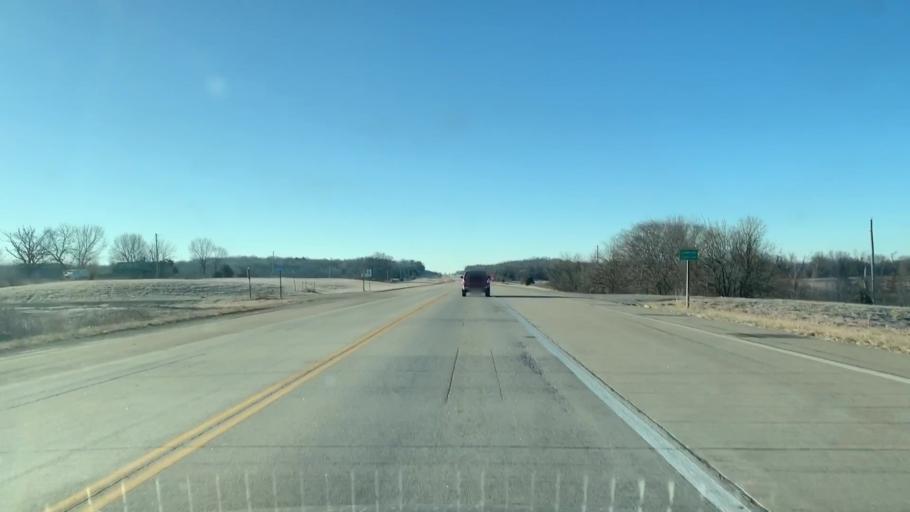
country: US
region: Kansas
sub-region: Crawford County
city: Arma
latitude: 37.6738
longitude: -94.7036
